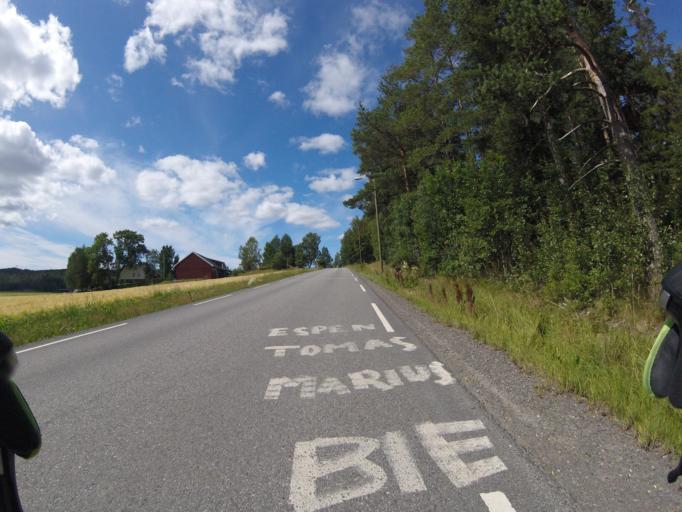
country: NO
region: Akershus
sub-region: Lorenskog
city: Kjenn
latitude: 59.9063
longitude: 10.9623
